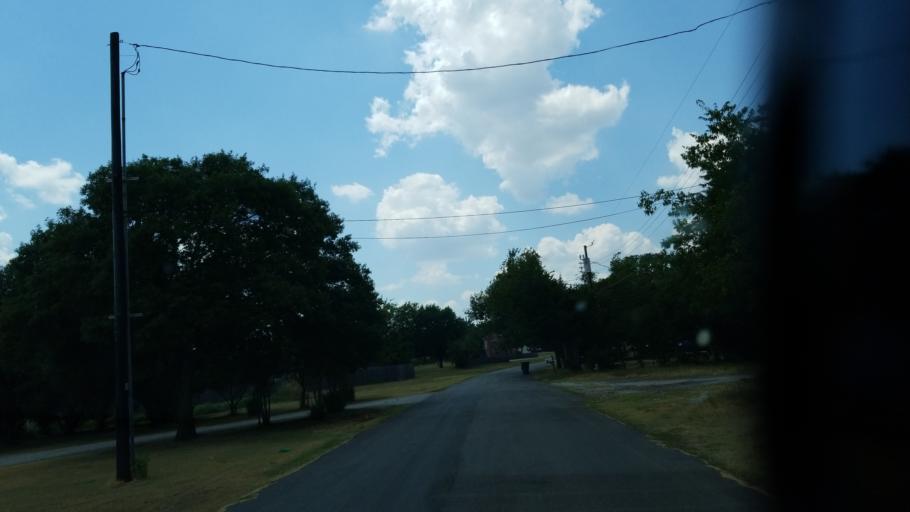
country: US
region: Texas
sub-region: Dallas County
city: Duncanville
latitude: 32.6750
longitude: -96.8876
